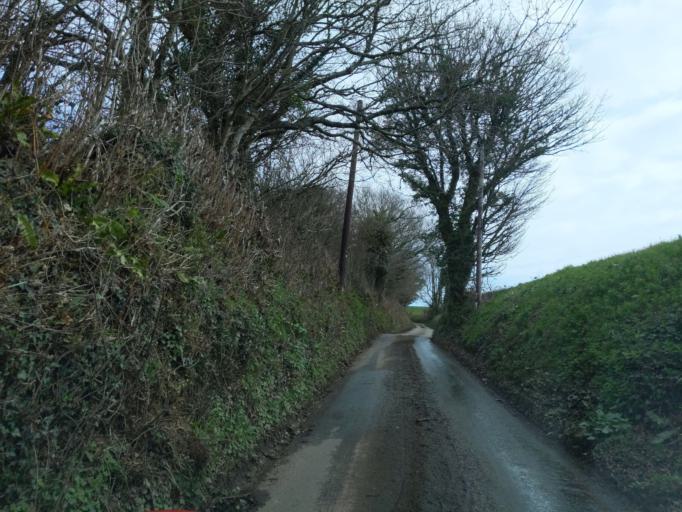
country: GB
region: England
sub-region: Devon
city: Yealmpton
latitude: 50.3636
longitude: -4.0088
